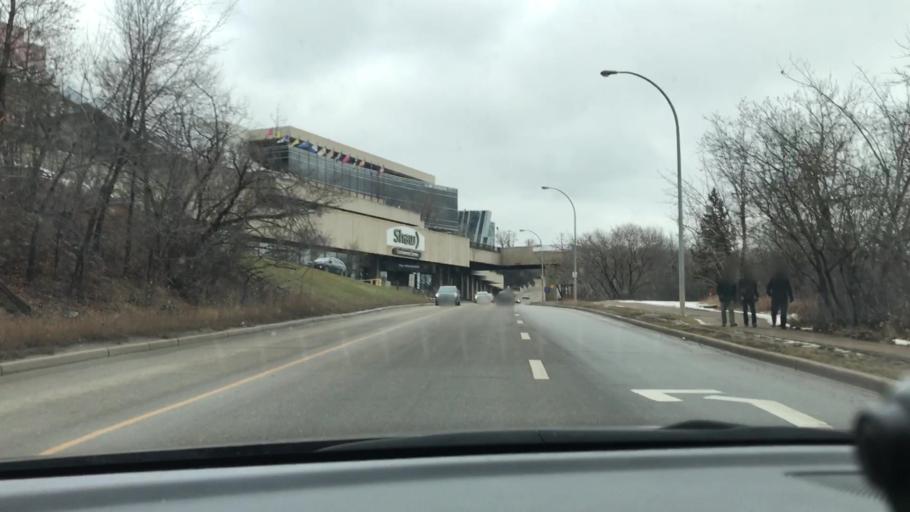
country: CA
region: Alberta
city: Edmonton
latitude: 53.5401
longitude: -113.4867
